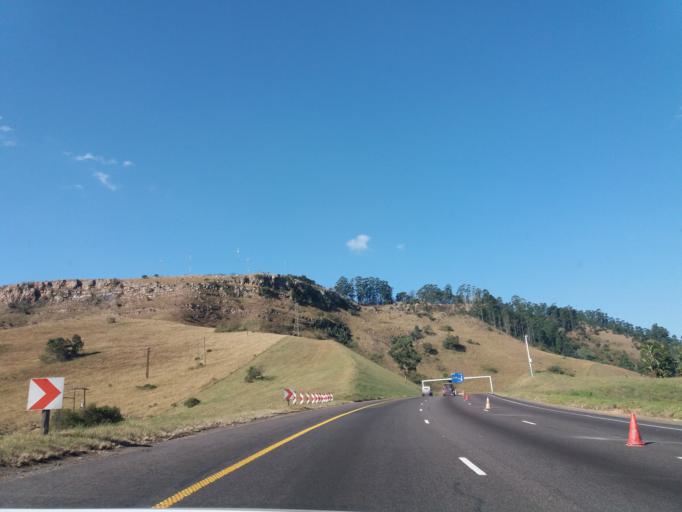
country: ZA
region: KwaZulu-Natal
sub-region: eThekwini Metropolitan Municipality
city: Mpumalanga
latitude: -29.7772
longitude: 30.7068
